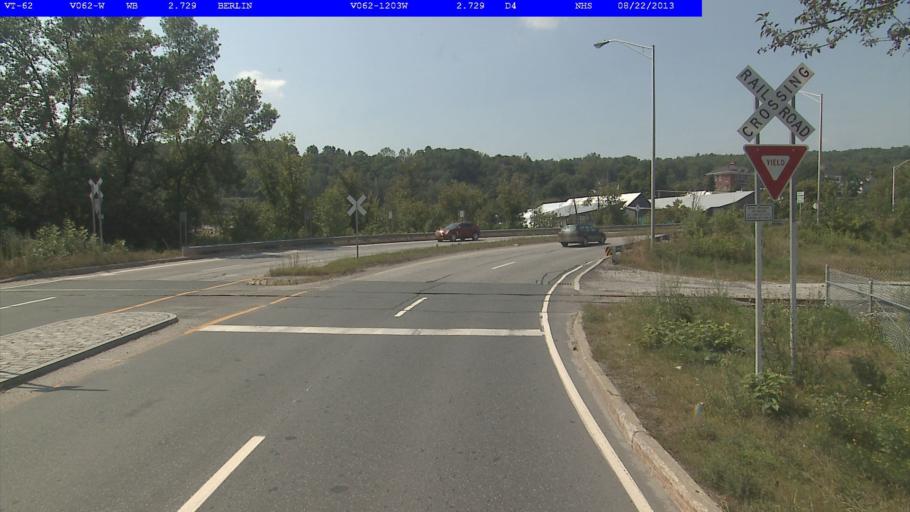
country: US
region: Vermont
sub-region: Washington County
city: Barre
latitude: 44.2022
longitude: -72.5085
